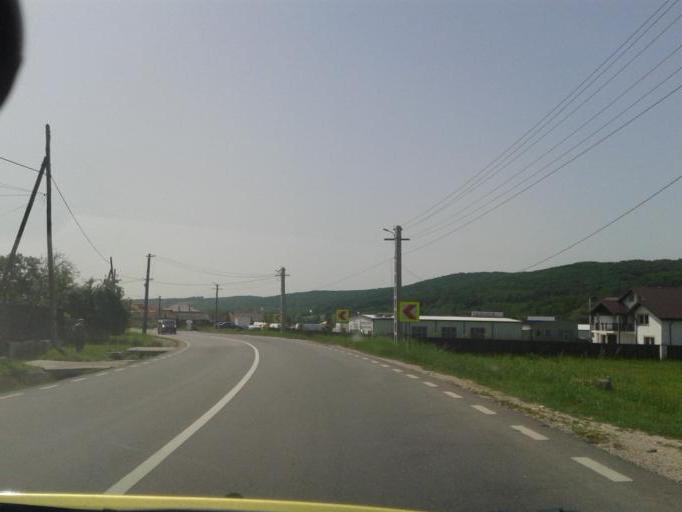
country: RO
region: Arges
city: Draganu-Olteni
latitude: 44.9140
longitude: 24.7207
